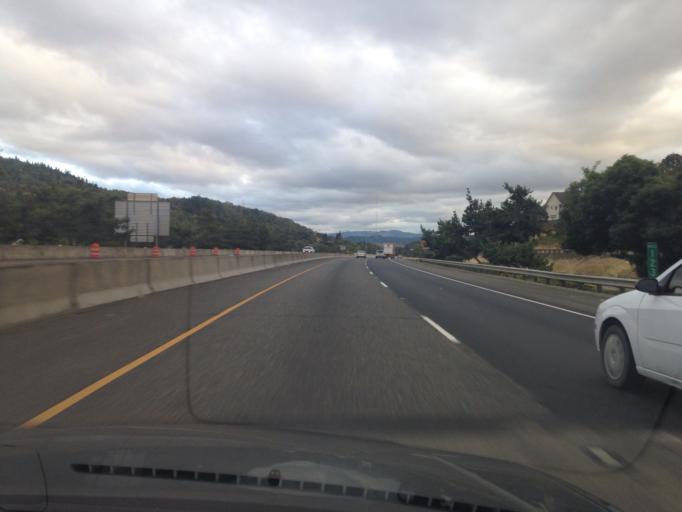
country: US
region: Oregon
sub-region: Douglas County
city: Roseburg
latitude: 43.1989
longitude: -123.3597
